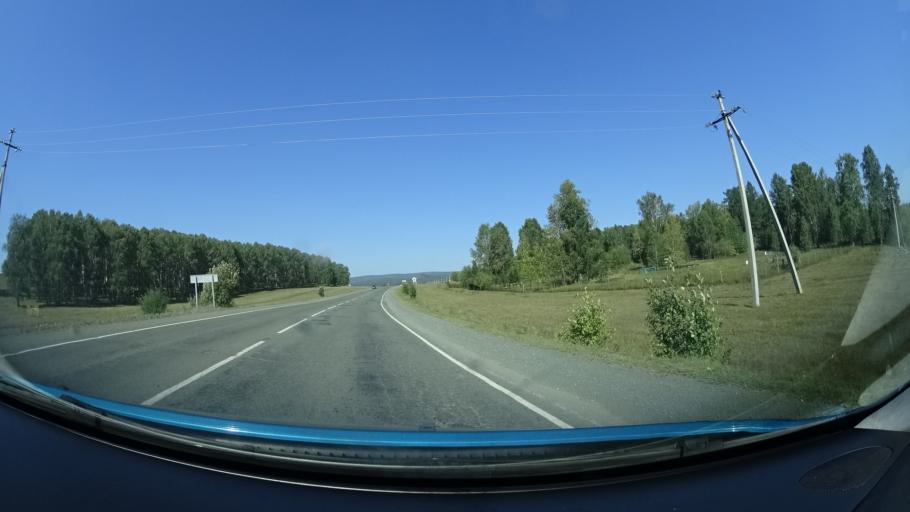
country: RU
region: Bashkortostan
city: Abzakovo
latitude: 53.8234
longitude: 58.6140
